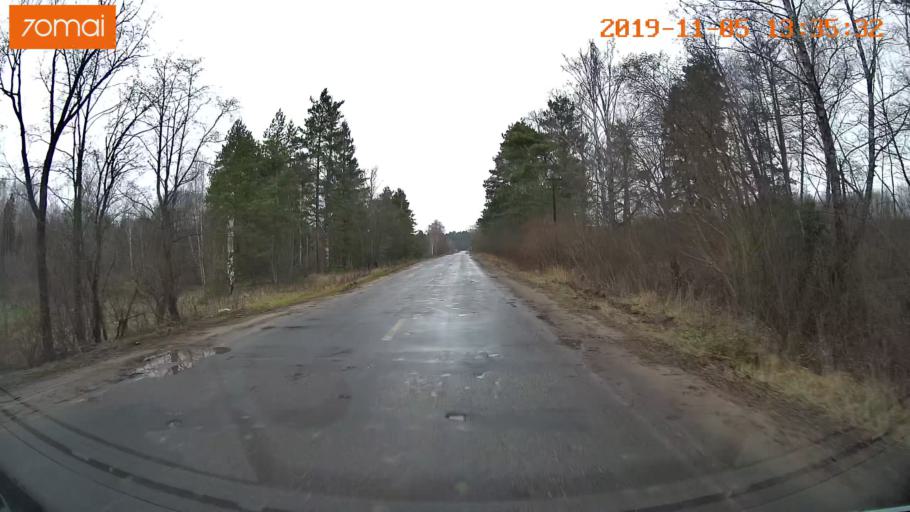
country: RU
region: Ivanovo
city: Shuya
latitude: 56.9085
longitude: 41.3869
